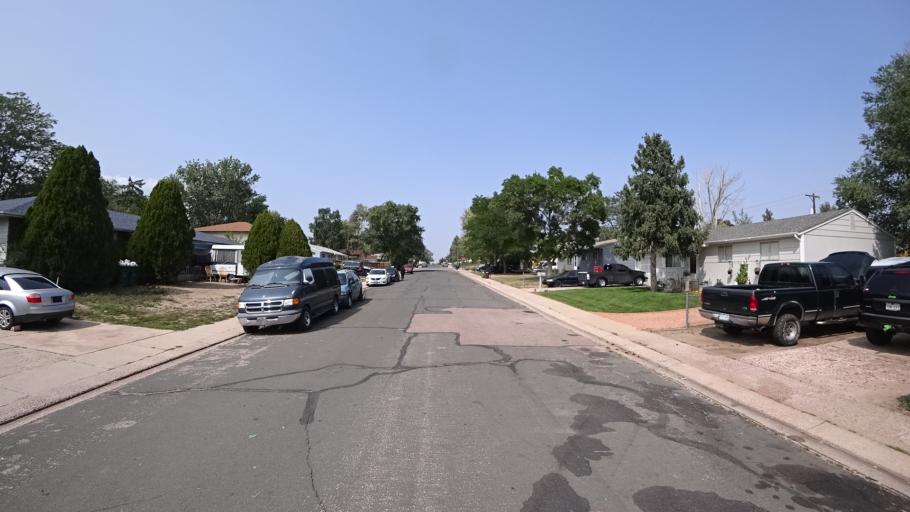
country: US
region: Colorado
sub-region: El Paso County
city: Stratmoor
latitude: 38.8037
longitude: -104.7727
